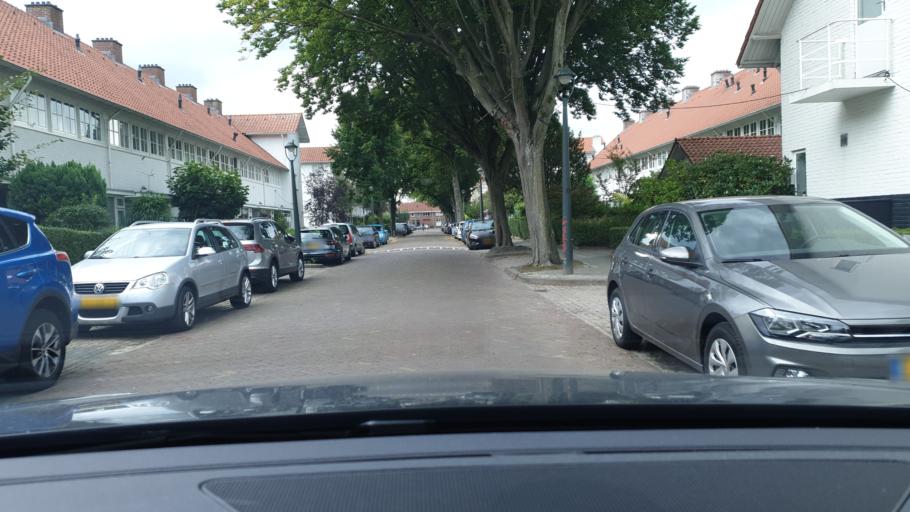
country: NL
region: North Brabant
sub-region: Gemeente Eindhoven
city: Lakerlopen
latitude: 51.4289
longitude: 5.4935
